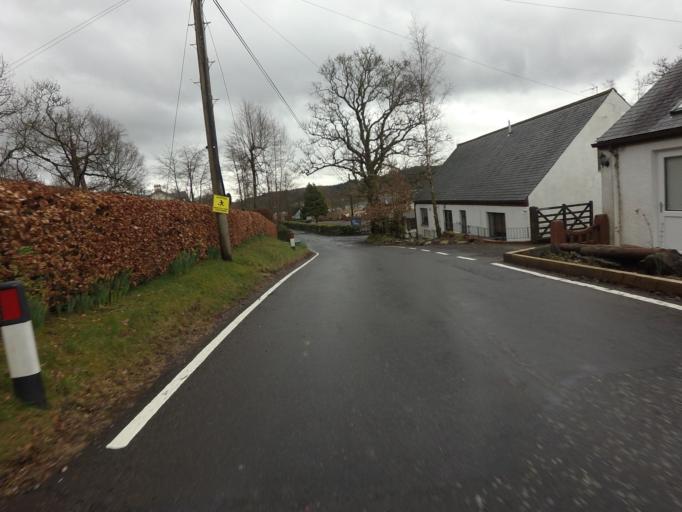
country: GB
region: Scotland
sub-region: Stirling
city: Killearn
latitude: 56.1884
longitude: -4.4919
